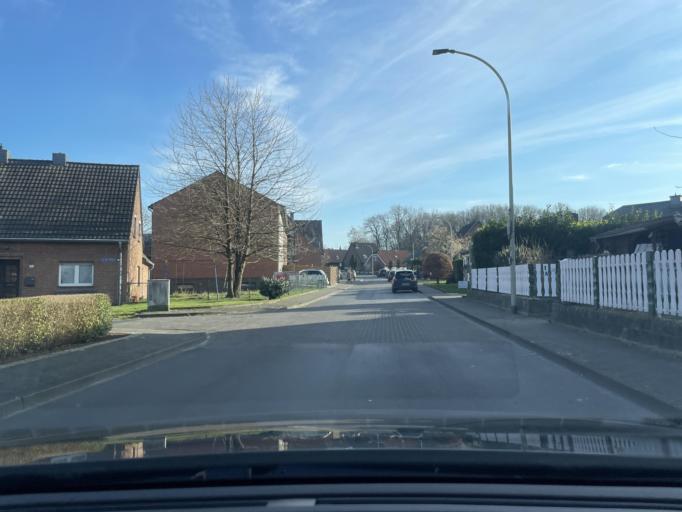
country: DE
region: North Rhine-Westphalia
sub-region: Regierungsbezirk Dusseldorf
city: Bruggen
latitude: 51.2312
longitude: 6.1554
